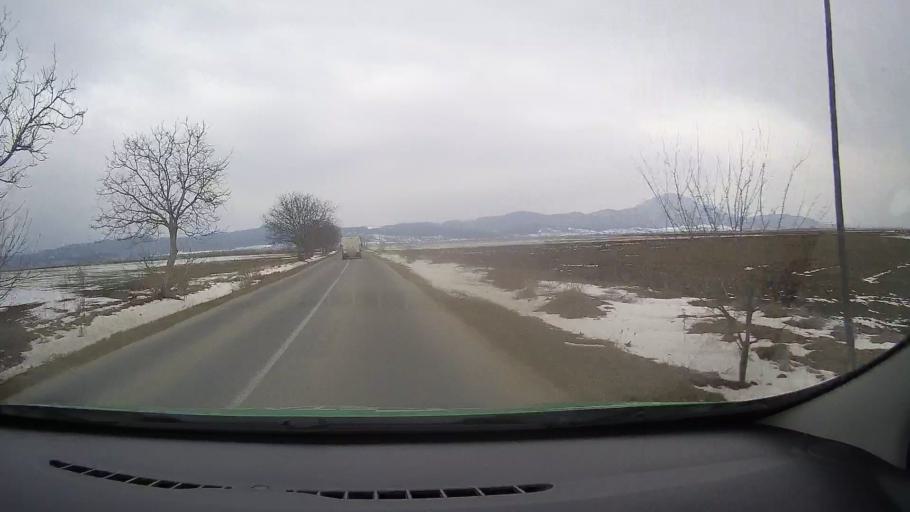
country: RO
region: Brasov
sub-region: Comuna Cristian
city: Cristian
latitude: 45.6328
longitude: 25.4579
